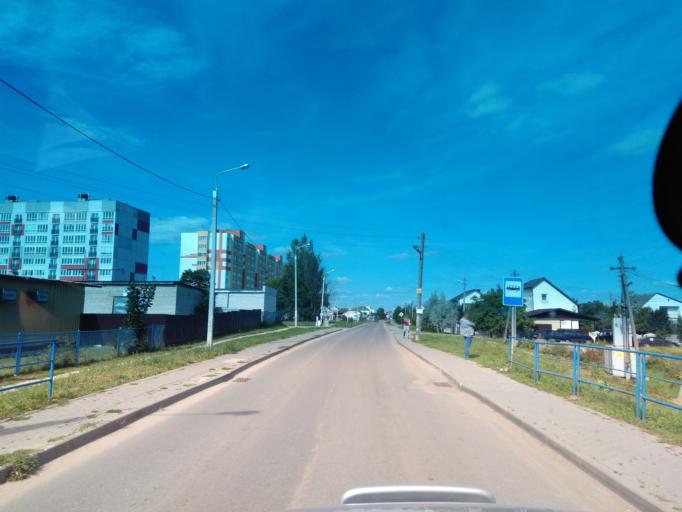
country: BY
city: Fanipol
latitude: 53.7500
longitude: 27.3344
